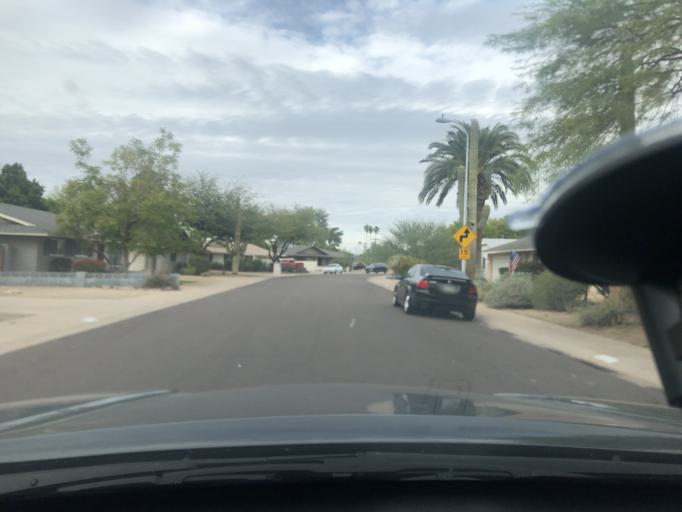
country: US
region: Arizona
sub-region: Maricopa County
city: Scottsdale
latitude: 33.4846
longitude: -111.9043
